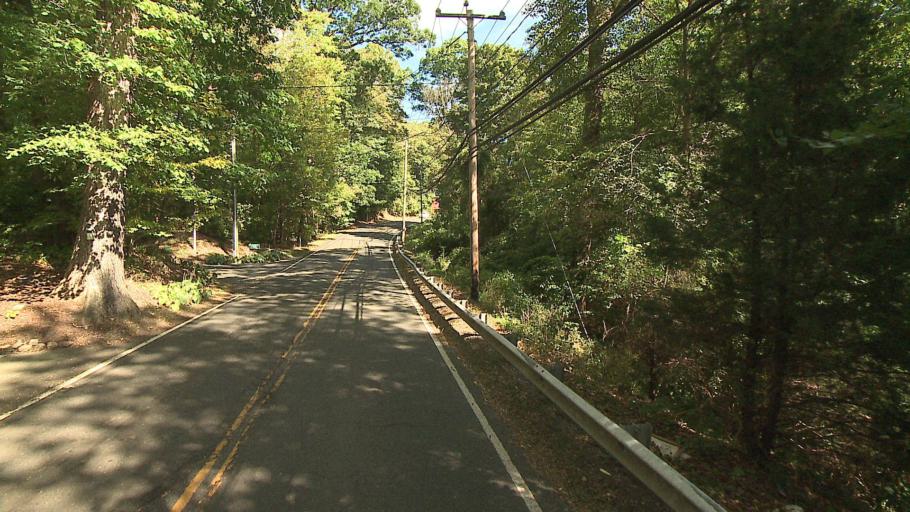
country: US
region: Connecticut
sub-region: Fairfield County
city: New Canaan
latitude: 41.1549
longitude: -73.4768
